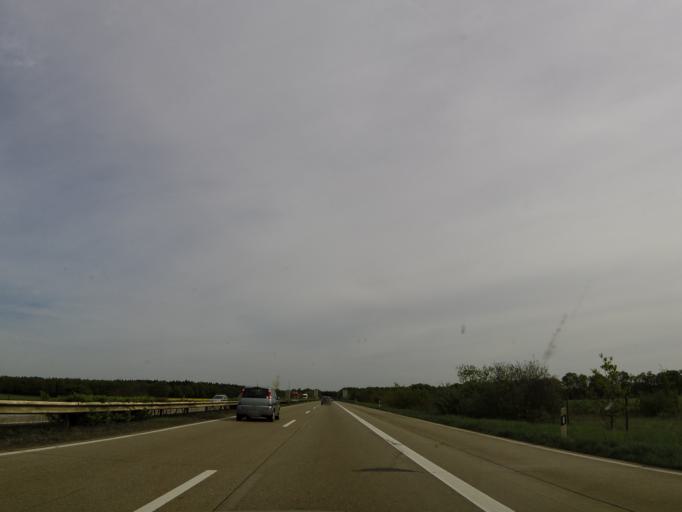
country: DE
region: Lower Saxony
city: Bad Fallingbostel
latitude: 52.8309
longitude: 9.6855
